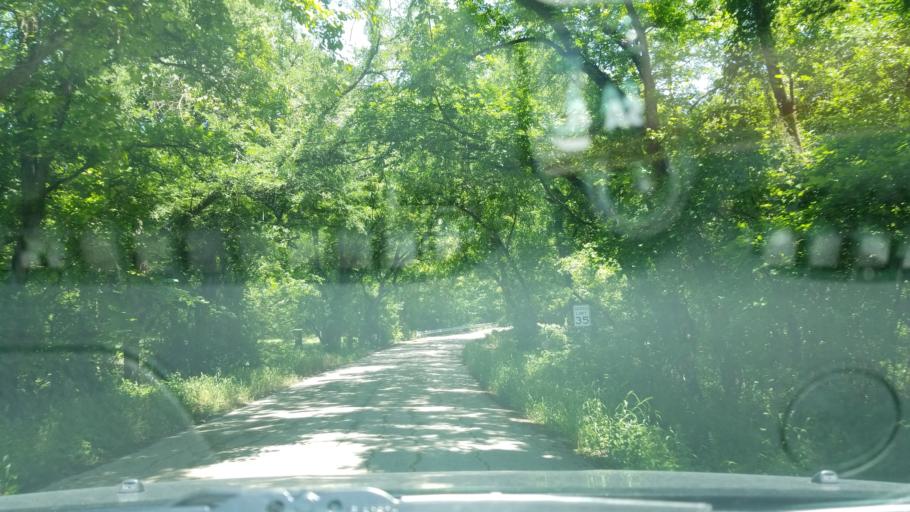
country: US
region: Texas
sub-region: Denton County
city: Sanger
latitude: 33.3507
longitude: -97.2026
